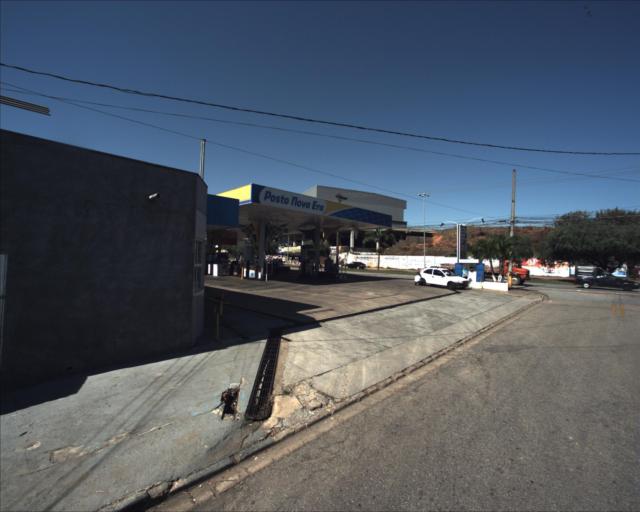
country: BR
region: Sao Paulo
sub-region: Sorocaba
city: Sorocaba
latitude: -23.4706
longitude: -47.4904
